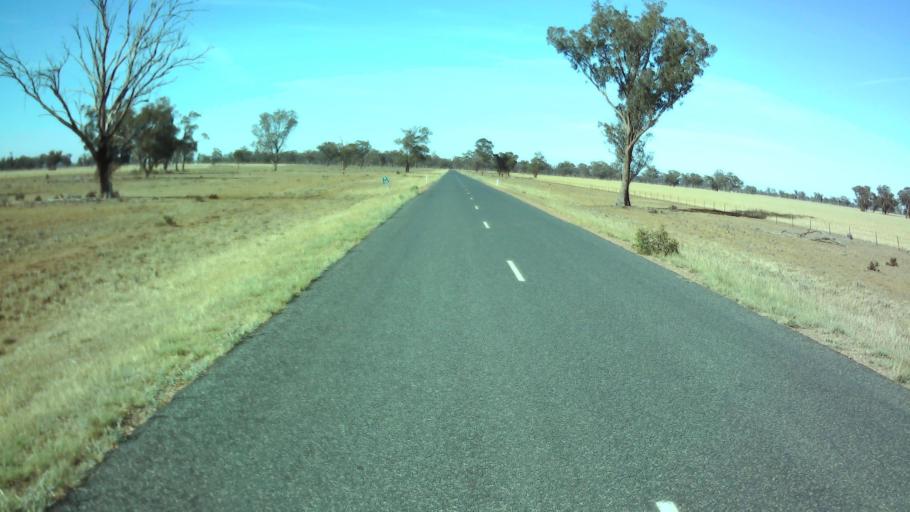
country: AU
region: New South Wales
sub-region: Weddin
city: Grenfell
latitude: -34.0526
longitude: 147.9175
